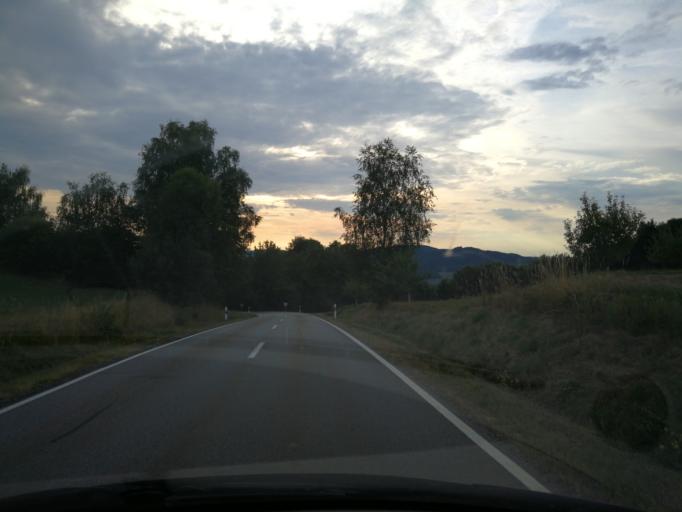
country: DE
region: Bavaria
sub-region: Lower Bavaria
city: Haibach
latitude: 49.0277
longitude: 12.7465
